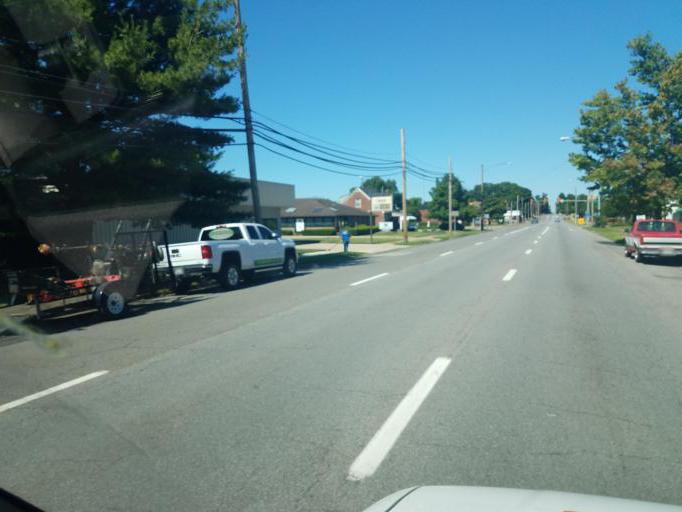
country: US
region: West Virginia
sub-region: Cabell County
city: Huntington
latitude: 38.4300
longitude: -82.3979
